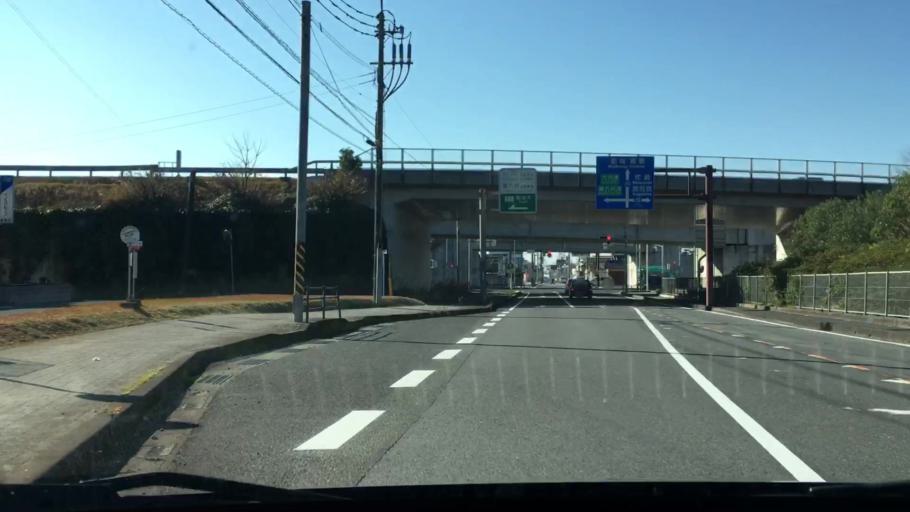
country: JP
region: Kagoshima
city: Kajiki
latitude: 31.7467
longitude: 130.6705
